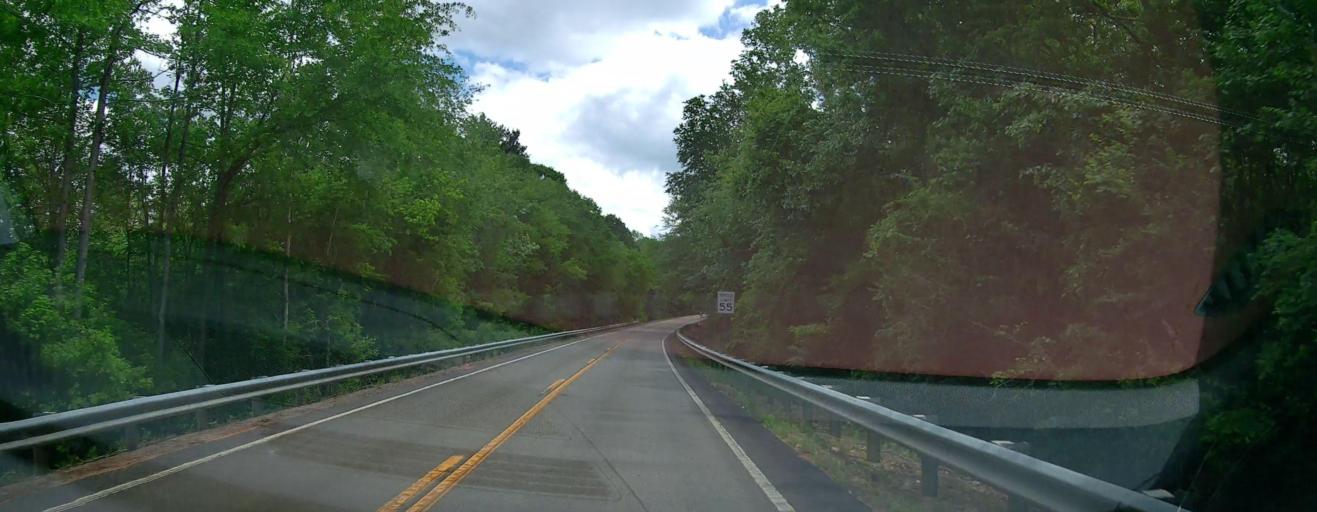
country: US
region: Georgia
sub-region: Dodge County
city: Chester
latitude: 32.5360
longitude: -83.1983
